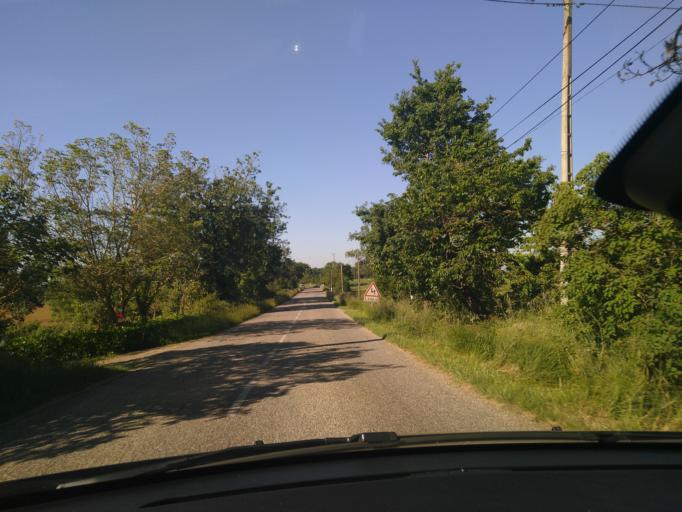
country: FR
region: Midi-Pyrenees
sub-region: Departement du Gers
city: Gimont
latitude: 43.6996
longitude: 0.8769
